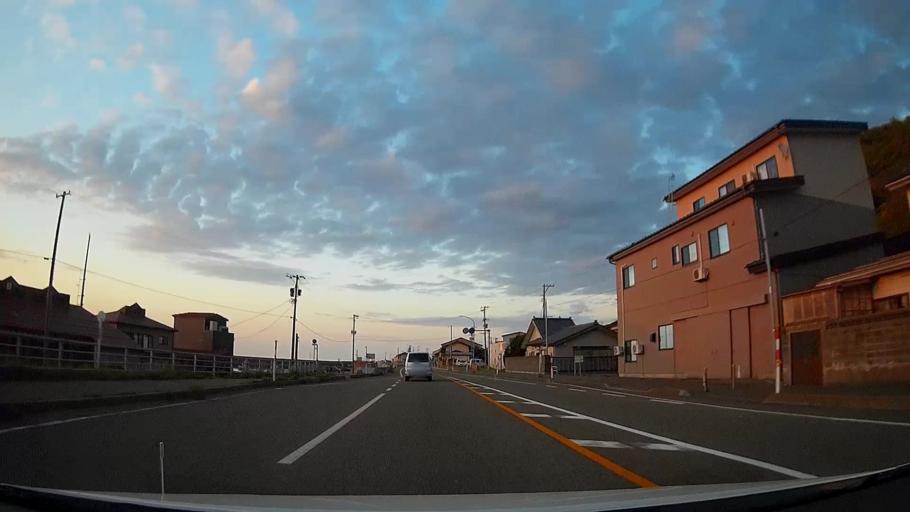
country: JP
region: Niigata
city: Joetsu
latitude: 37.1649
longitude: 138.0887
